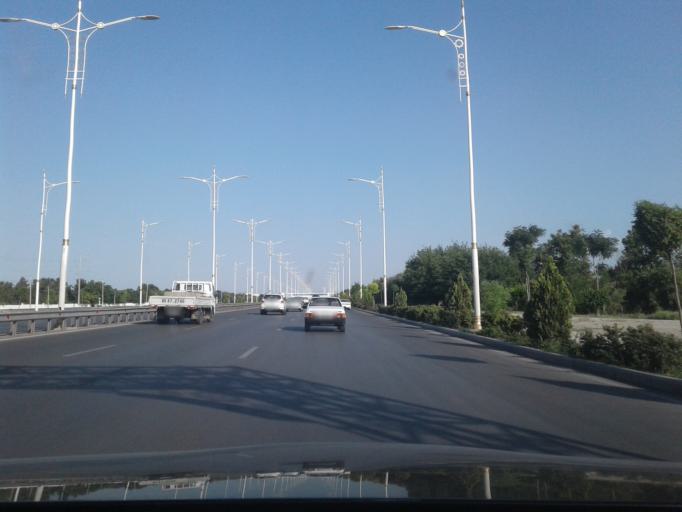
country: TM
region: Ahal
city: Ashgabat
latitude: 37.9740
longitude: 58.3473
